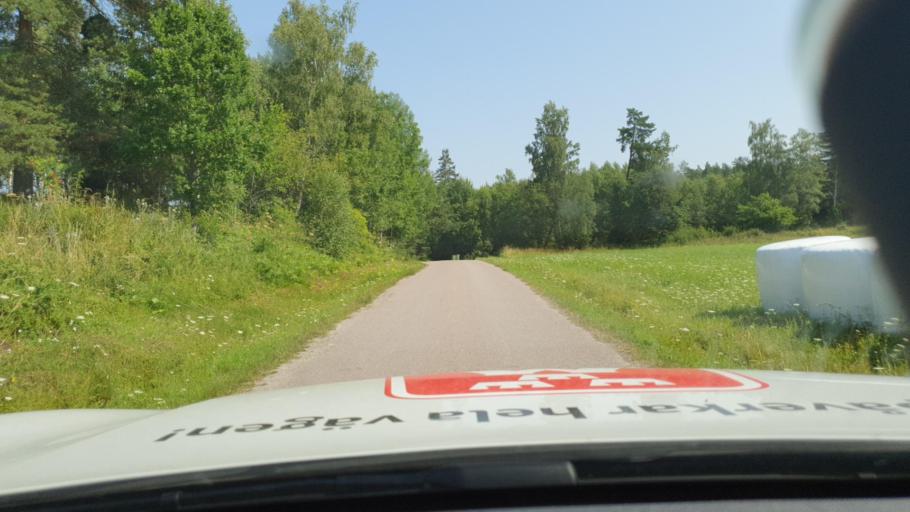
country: SE
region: Soedermanland
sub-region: Strangnas Kommun
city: Stallarholmen
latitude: 59.4060
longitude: 17.3060
